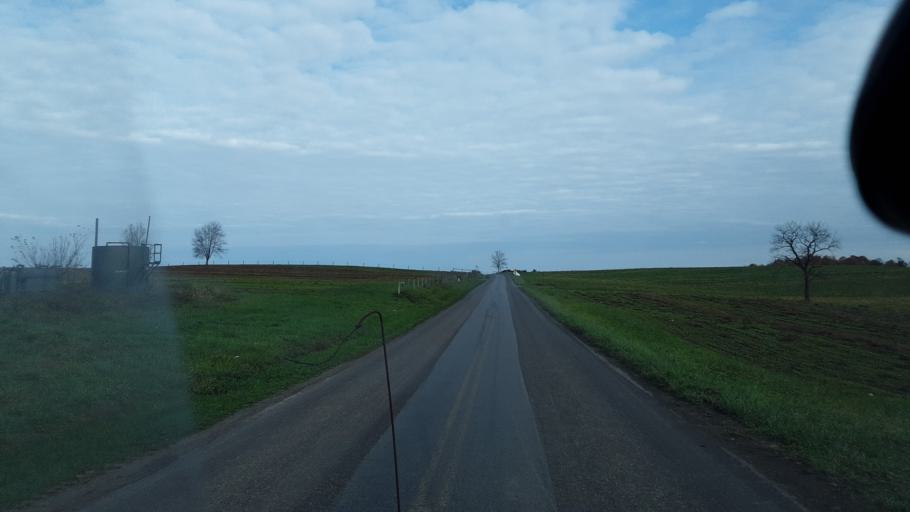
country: US
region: Ohio
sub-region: Tuscarawas County
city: Sugarcreek
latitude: 40.4613
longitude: -81.7759
